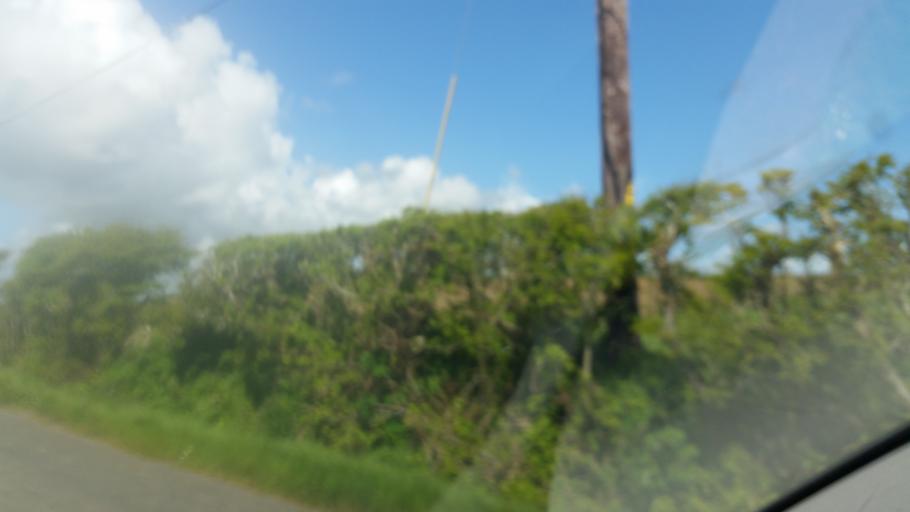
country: IE
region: Munster
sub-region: Waterford
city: Dunmore East
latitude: 52.1697
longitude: -6.8958
